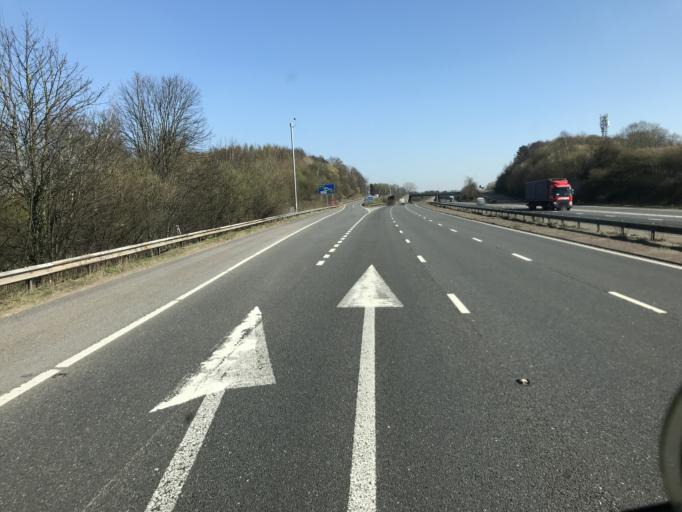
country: GB
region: England
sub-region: Borough of Halton
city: Daresbury
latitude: 53.3246
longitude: -2.6497
